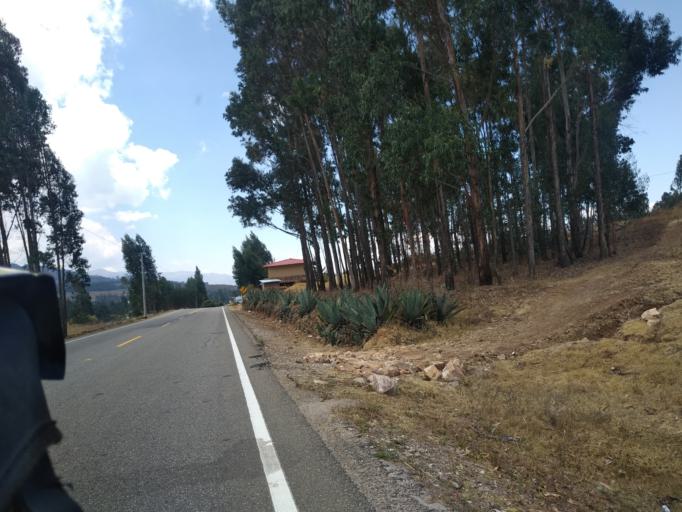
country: PE
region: Cajamarca
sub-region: San Marcos
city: San Marcos
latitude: -7.2804
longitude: -78.2320
